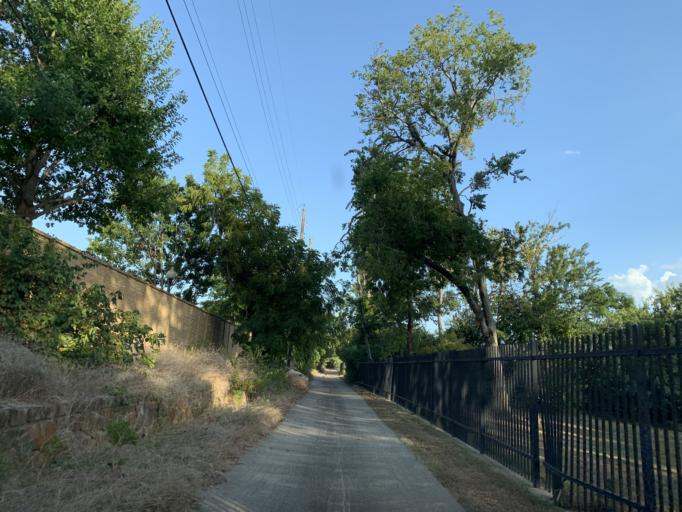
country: US
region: Texas
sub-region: Dallas County
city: Dallas
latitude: 32.7563
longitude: -96.7475
